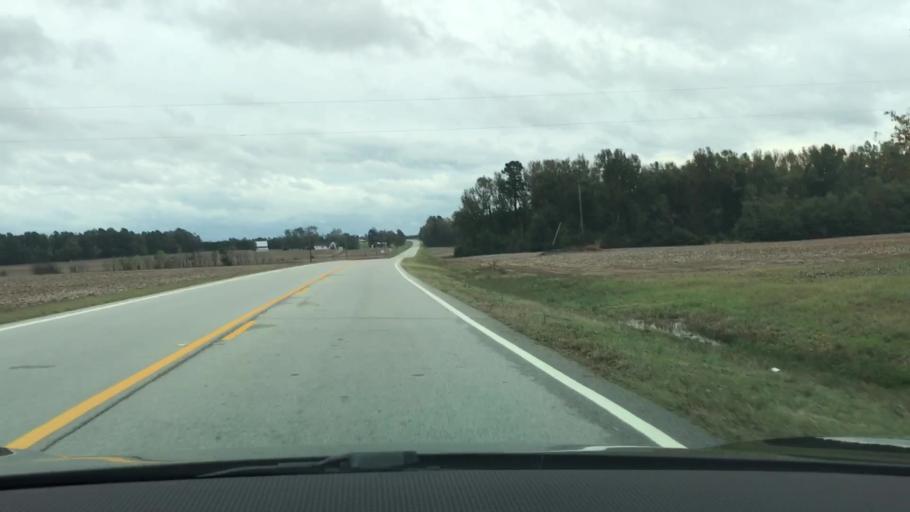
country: US
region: Georgia
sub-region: Jefferson County
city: Wrens
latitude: 33.2585
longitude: -82.4729
